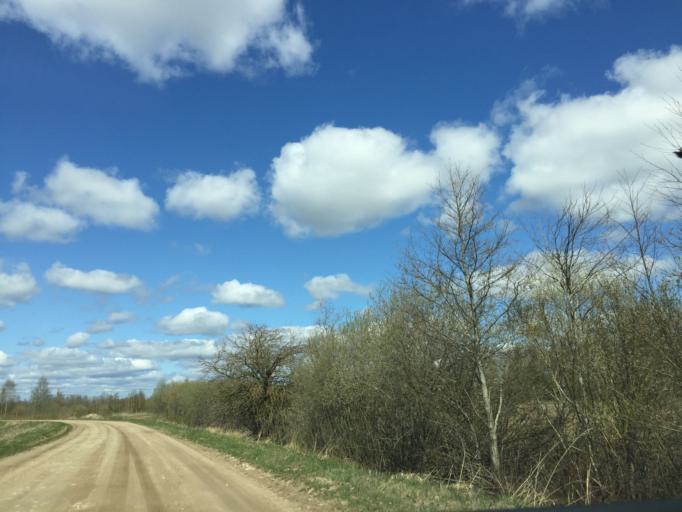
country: LV
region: Vilanu
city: Vilani
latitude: 56.6668
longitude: 27.1039
